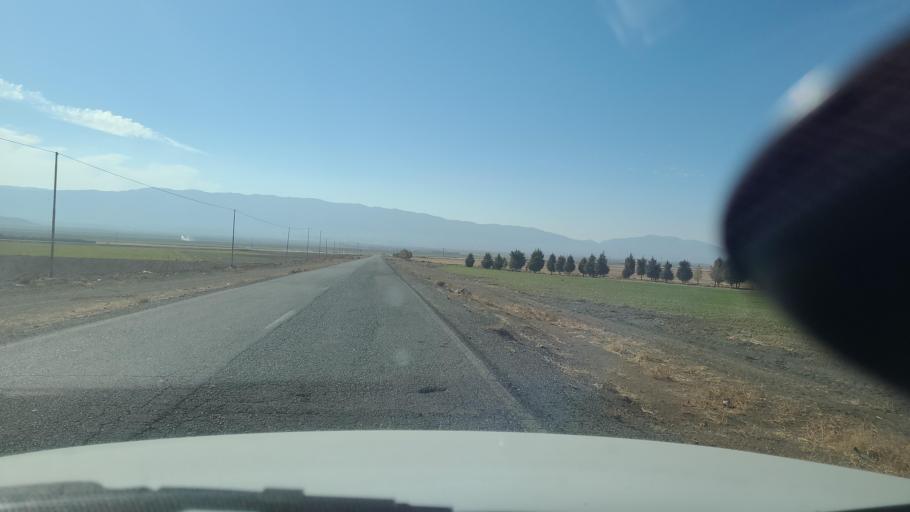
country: IR
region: Razavi Khorasan
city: Dowlatabad
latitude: 35.6052
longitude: 59.4638
